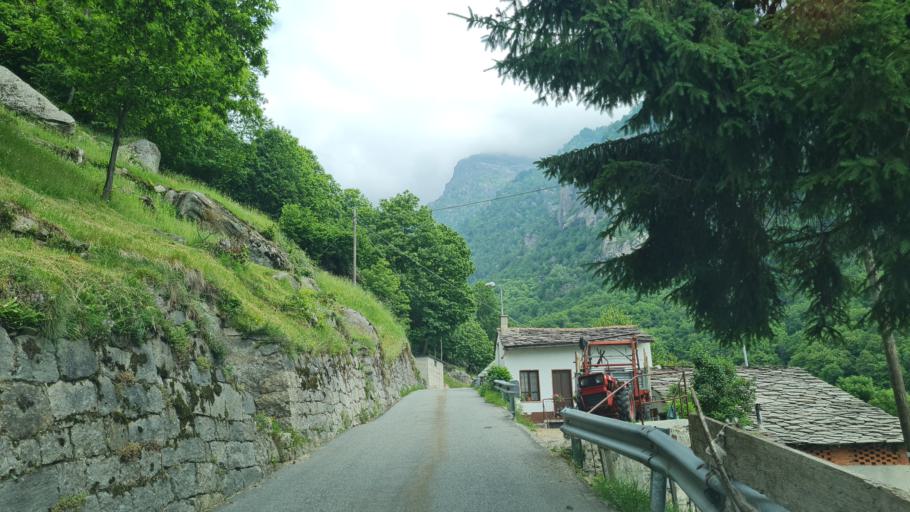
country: IT
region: Piedmont
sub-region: Provincia di Torino
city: Locana
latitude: 45.4403
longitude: 7.4171
